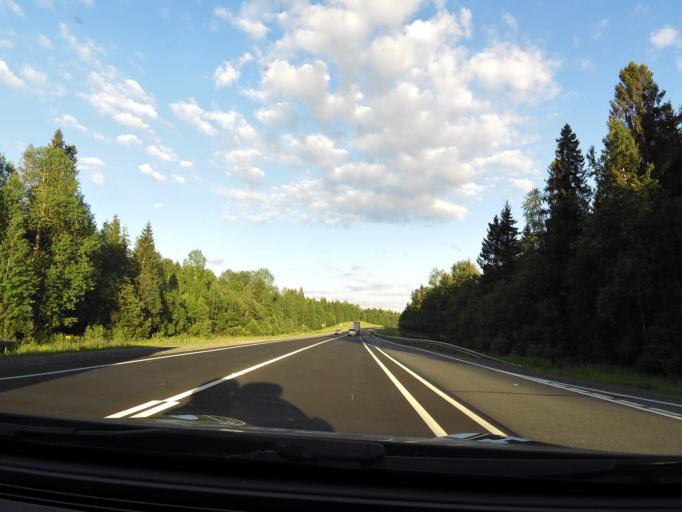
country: RU
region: Vologda
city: Gryazovets
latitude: 59.0456
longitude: 40.0958
